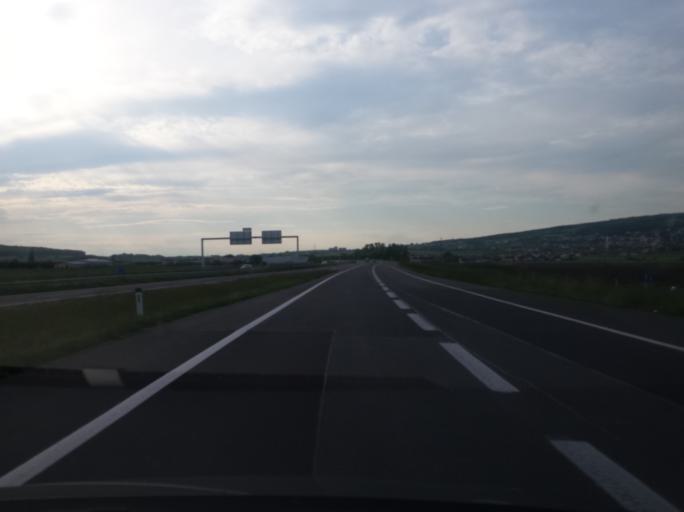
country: AT
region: Burgenland
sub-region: Eisenstadt-Umgebung
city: Wulkaprodersdorf
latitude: 47.8190
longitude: 16.4924
